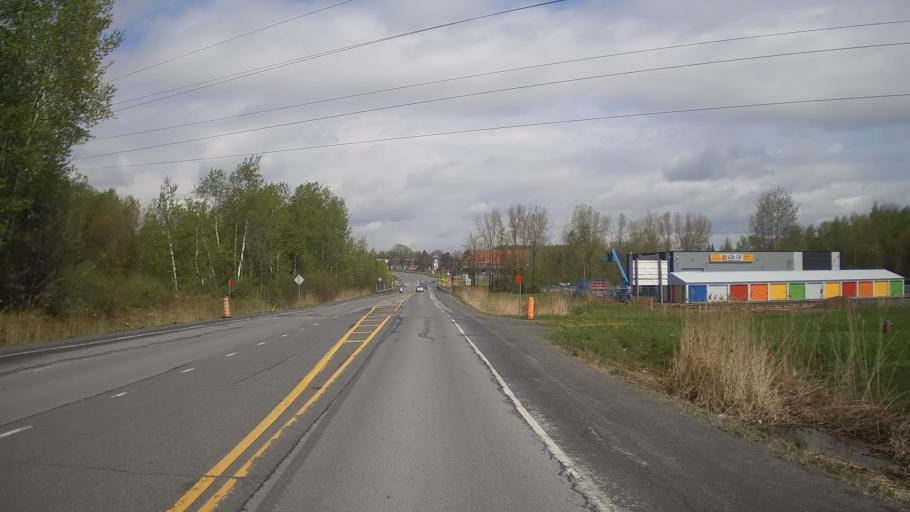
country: CA
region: Quebec
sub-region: Monteregie
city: Cowansville
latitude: 45.2047
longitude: -72.7663
